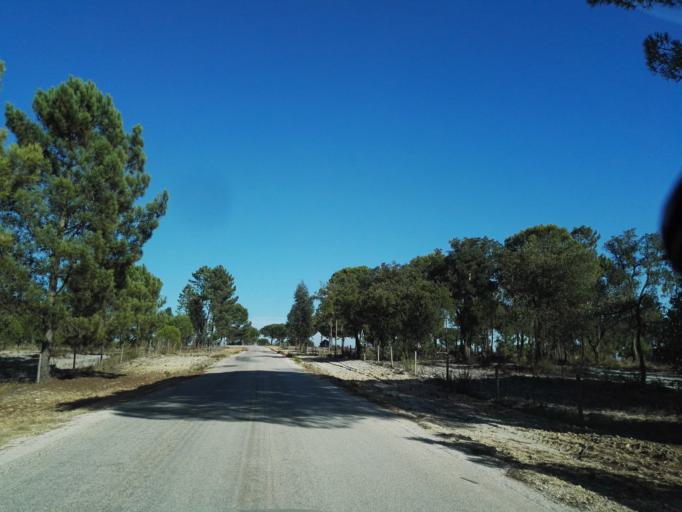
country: PT
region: Santarem
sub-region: Benavente
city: Poceirao
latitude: 38.8818
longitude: -8.7260
